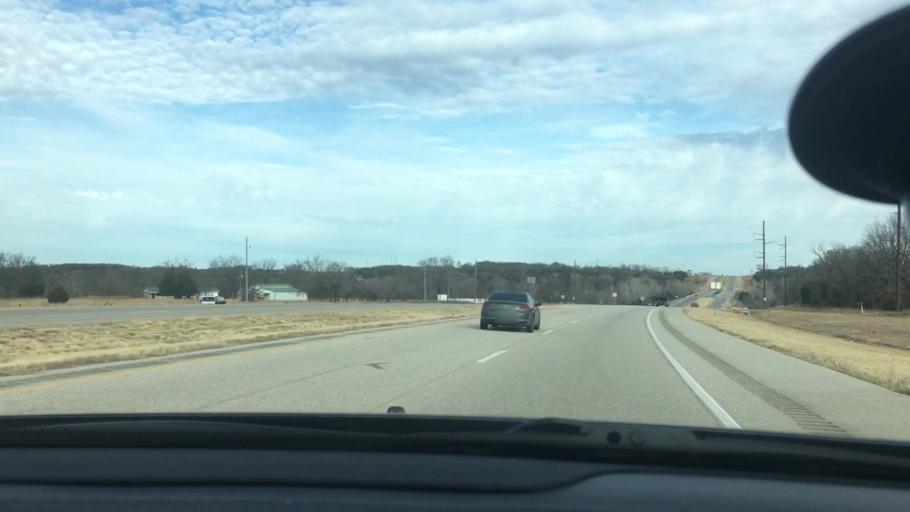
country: US
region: Oklahoma
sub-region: Pontotoc County
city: Byng
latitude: 34.9246
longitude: -96.6839
